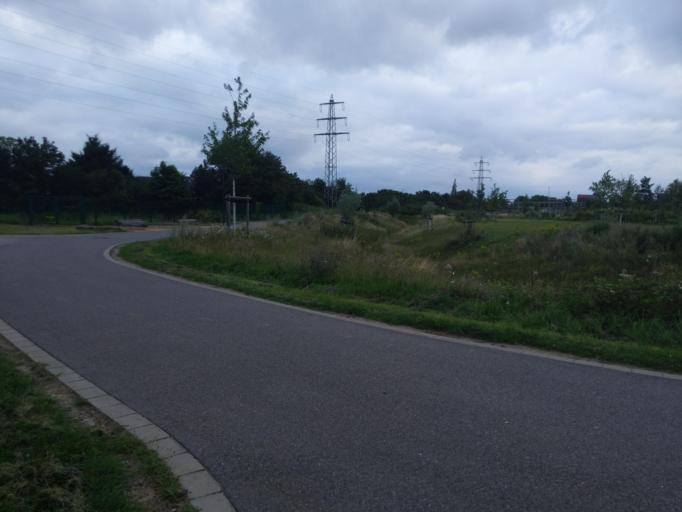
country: DE
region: North Rhine-Westphalia
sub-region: Regierungsbezirk Dusseldorf
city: Meerbusch
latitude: 51.2426
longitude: 6.7086
